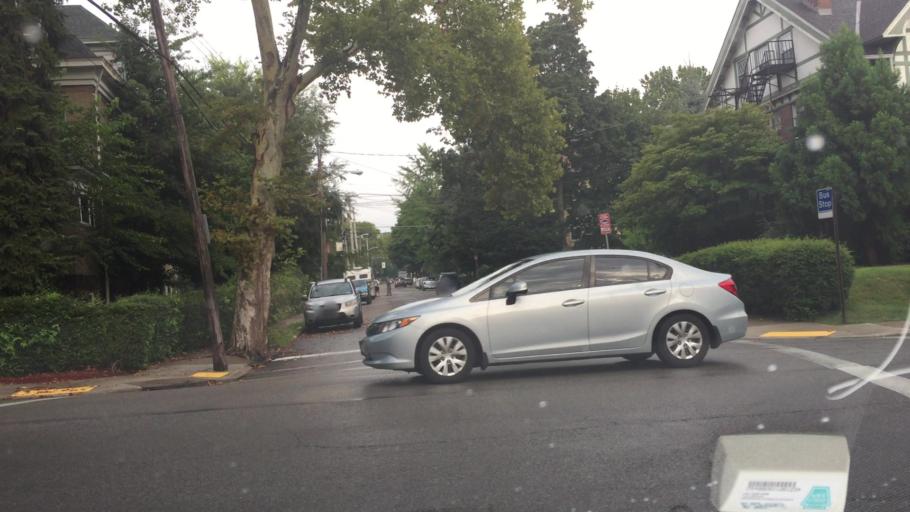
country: US
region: Pennsylvania
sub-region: Allegheny County
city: Sharpsburg
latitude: 40.4755
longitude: -79.9247
